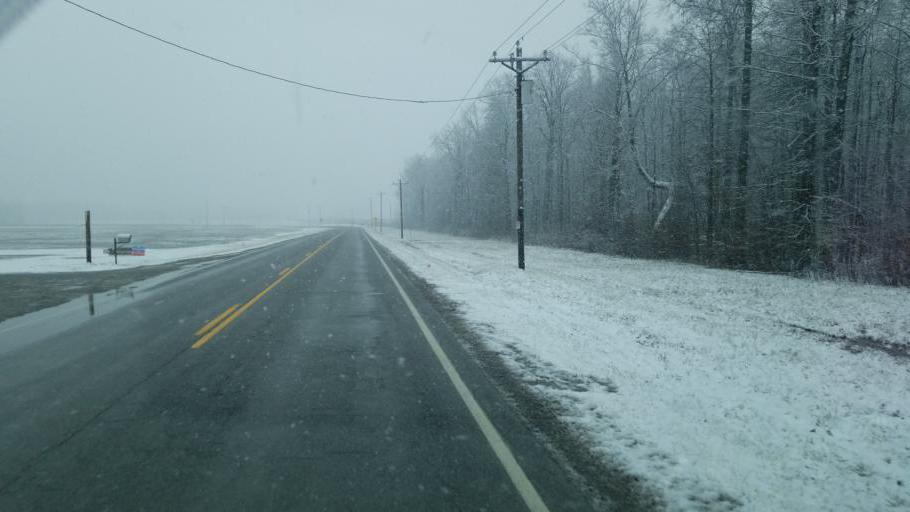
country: US
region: Ohio
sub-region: Champaign County
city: North Lewisburg
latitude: 40.2828
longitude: -83.4977
